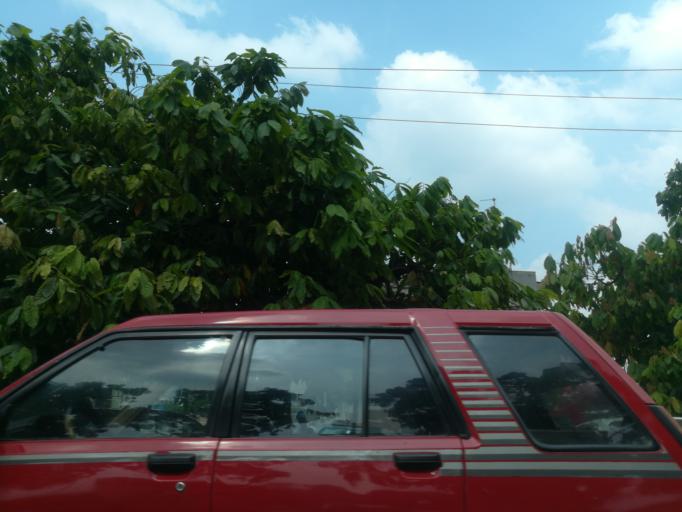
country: NG
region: Oyo
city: Ibadan
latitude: 7.4113
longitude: 3.9065
